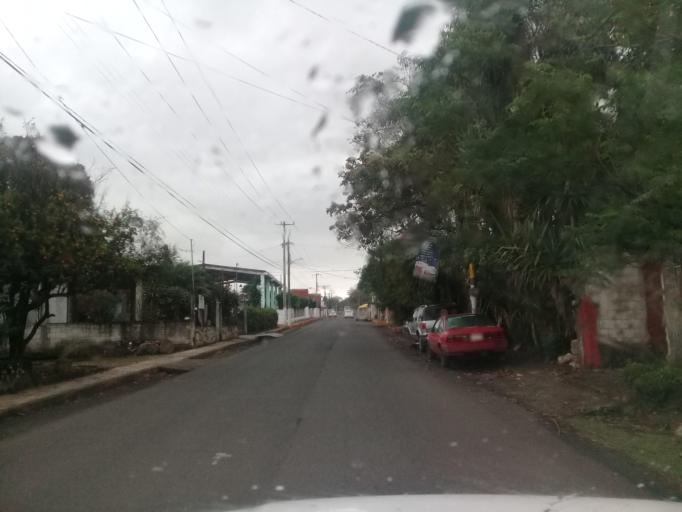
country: MX
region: Veracruz
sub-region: Cordoba
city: Veinte de Noviembre
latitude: 18.8632
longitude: -96.9536
